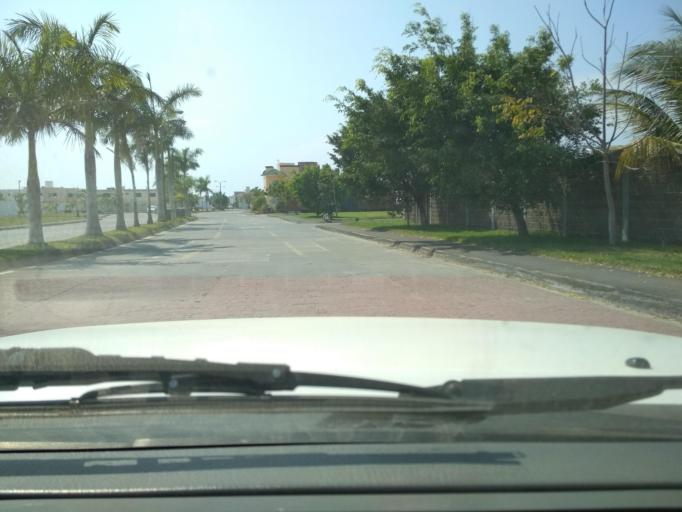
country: MX
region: Veracruz
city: Boca del Rio
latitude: 19.1044
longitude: -96.1223
